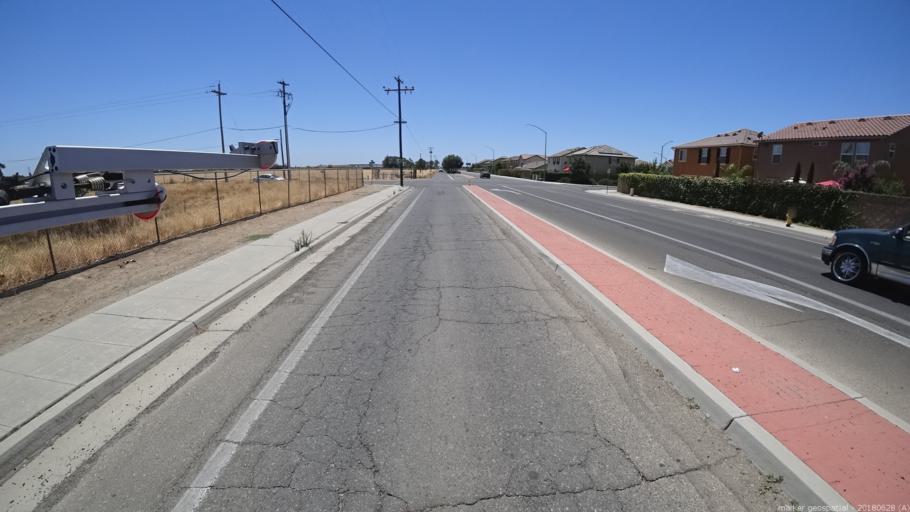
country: US
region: California
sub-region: Madera County
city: Parksdale
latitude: 36.9458
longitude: -120.0375
